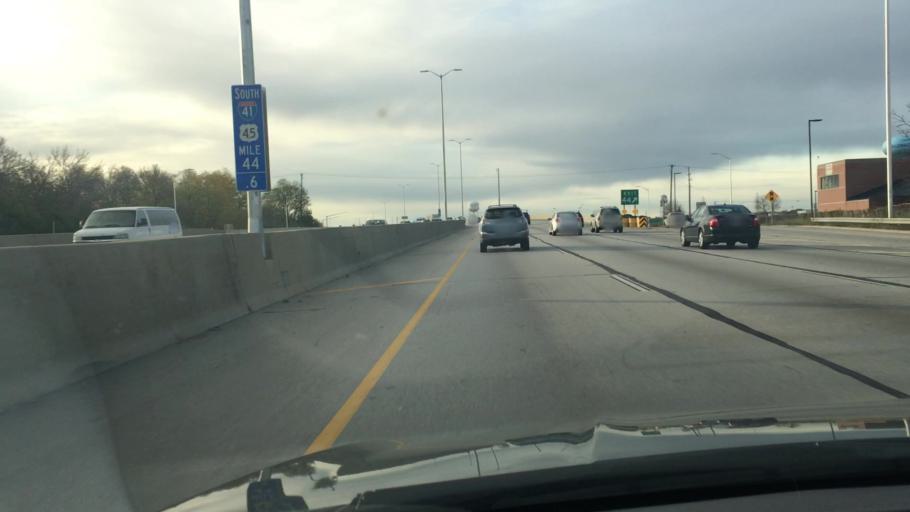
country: US
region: Wisconsin
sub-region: Waukesha County
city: Butler
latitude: 43.0912
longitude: -88.0582
